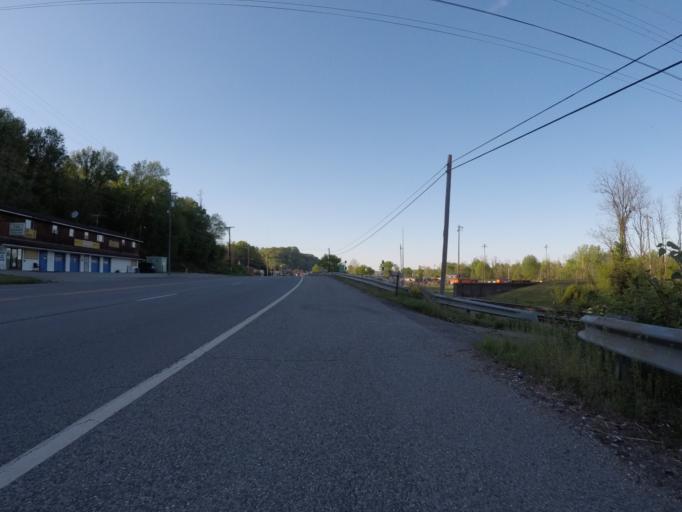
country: US
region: Kentucky
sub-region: Boyd County
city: Catlettsburg
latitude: 38.3979
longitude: -82.6008
